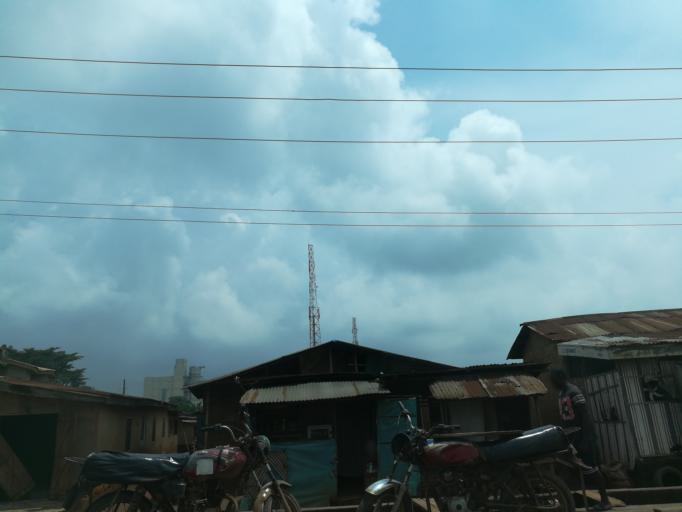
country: NG
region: Lagos
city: Ikorodu
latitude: 6.6800
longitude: 3.5133
